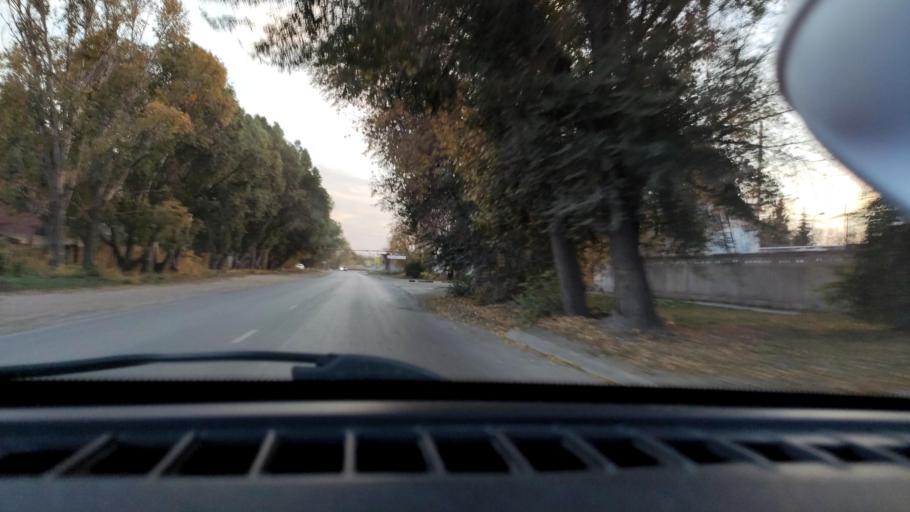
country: RU
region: Samara
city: Samara
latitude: 53.1857
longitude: 50.2446
